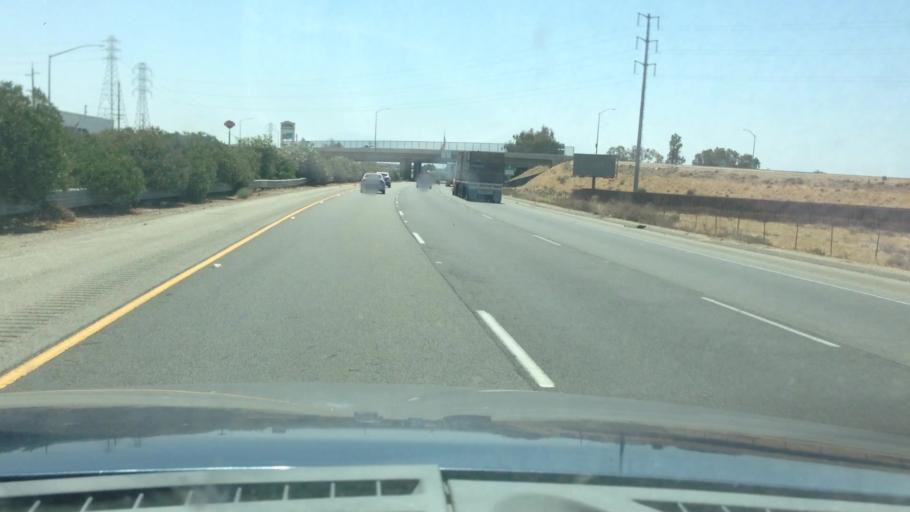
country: US
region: California
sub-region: Kern County
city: Greenacres
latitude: 35.4429
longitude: -119.0866
